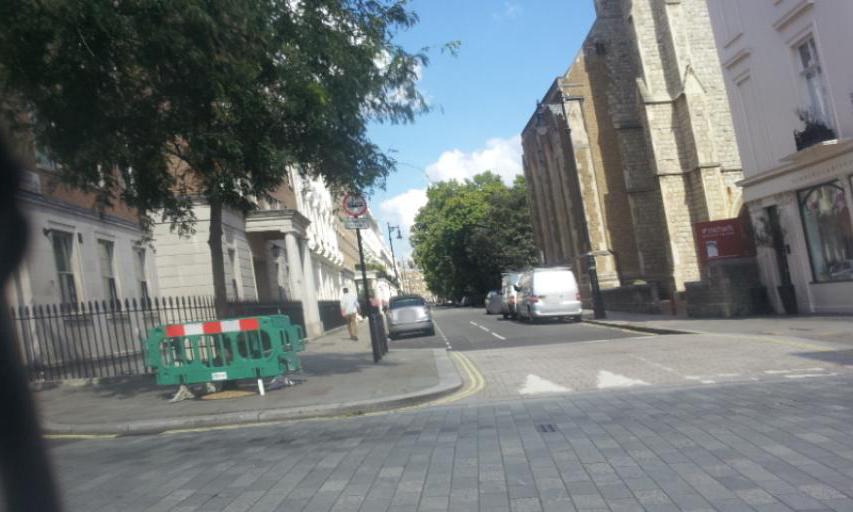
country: GB
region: England
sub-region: Greater London
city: Chelsea
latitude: 51.4941
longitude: -0.1517
